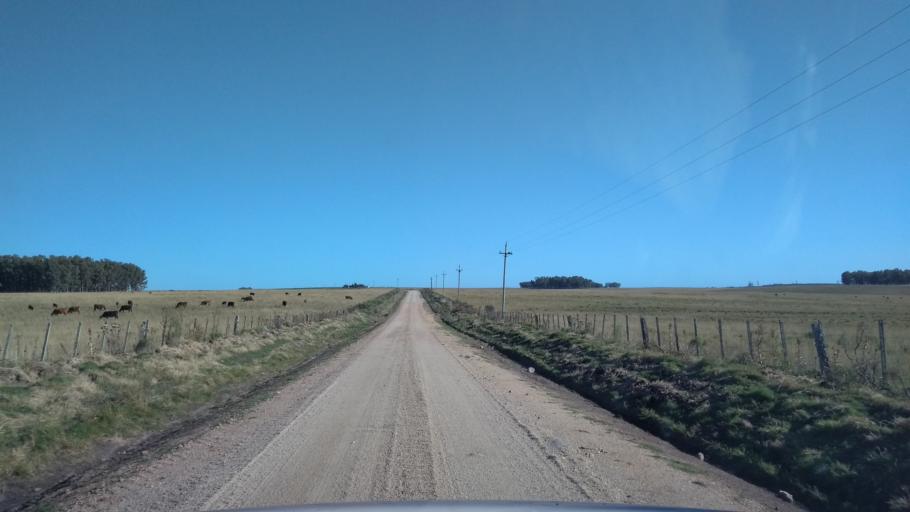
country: UY
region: Florida
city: Casupa
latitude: -34.0281
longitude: -55.7816
